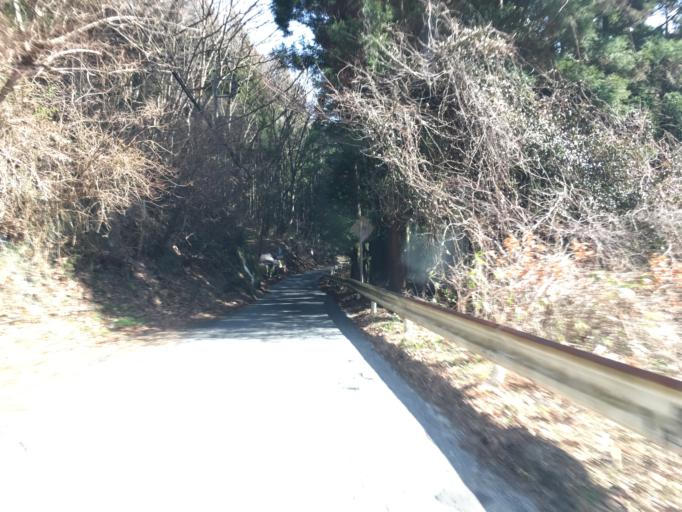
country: JP
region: Ibaraki
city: Takahagi
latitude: 36.8039
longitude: 140.6087
